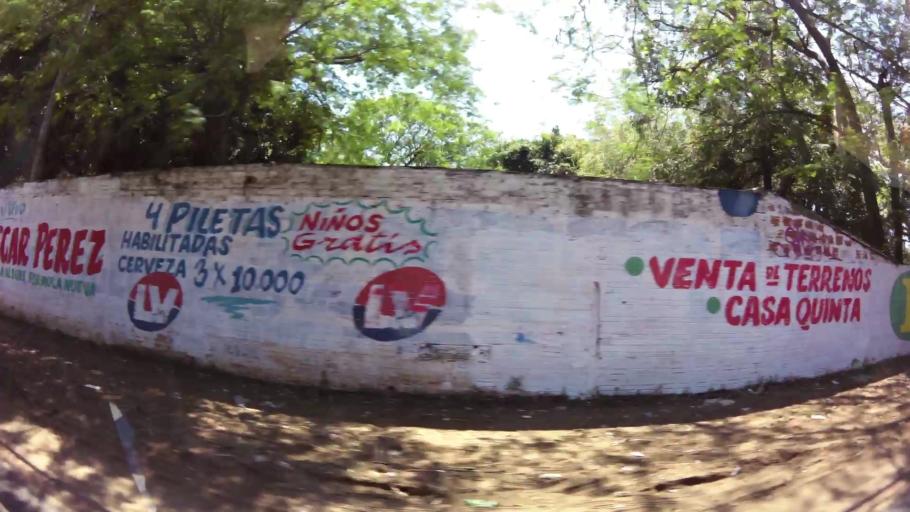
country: PY
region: Central
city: Nemby
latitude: -25.3944
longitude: -57.5427
